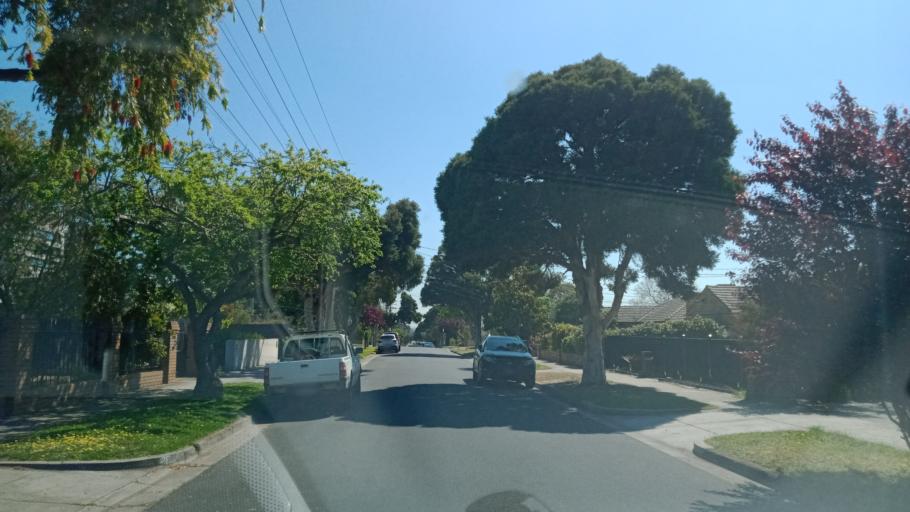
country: AU
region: Victoria
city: Murrumbeena
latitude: -37.9166
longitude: 145.0670
